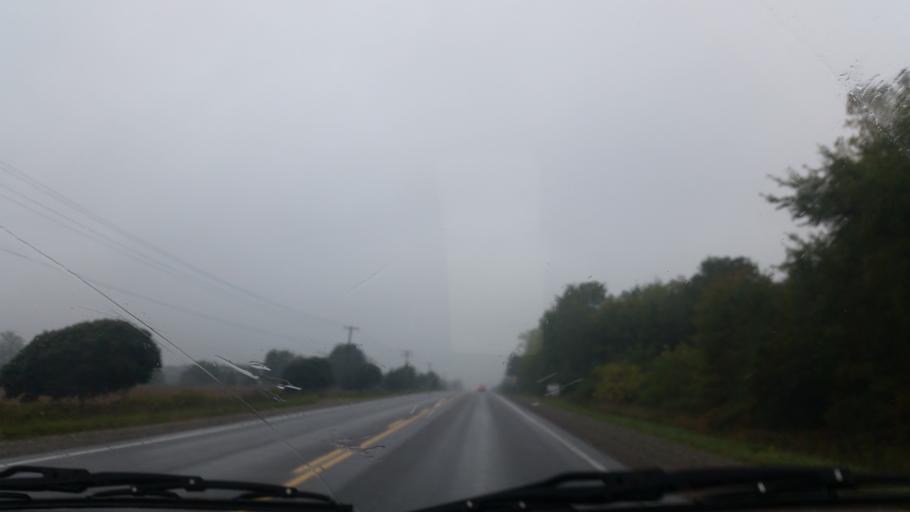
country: CA
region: Ontario
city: Stratford
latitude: 43.2755
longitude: -81.0636
